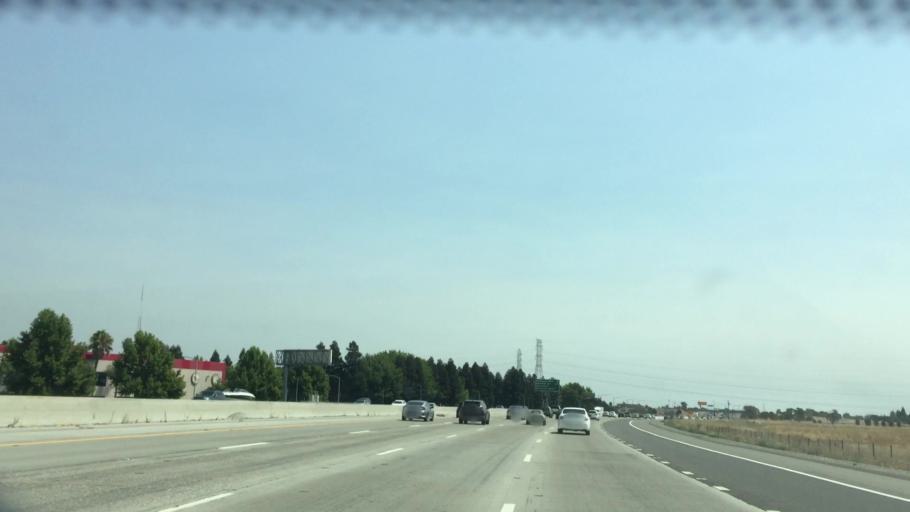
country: US
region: California
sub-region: Sacramento County
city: Sacramento
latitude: 38.6388
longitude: -121.4900
